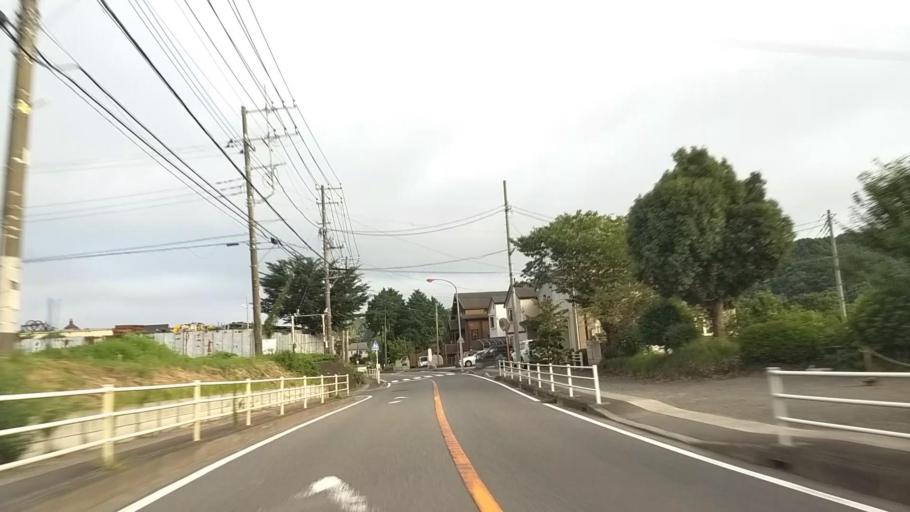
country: JP
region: Kanagawa
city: Atsugi
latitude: 35.4785
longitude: 139.3071
